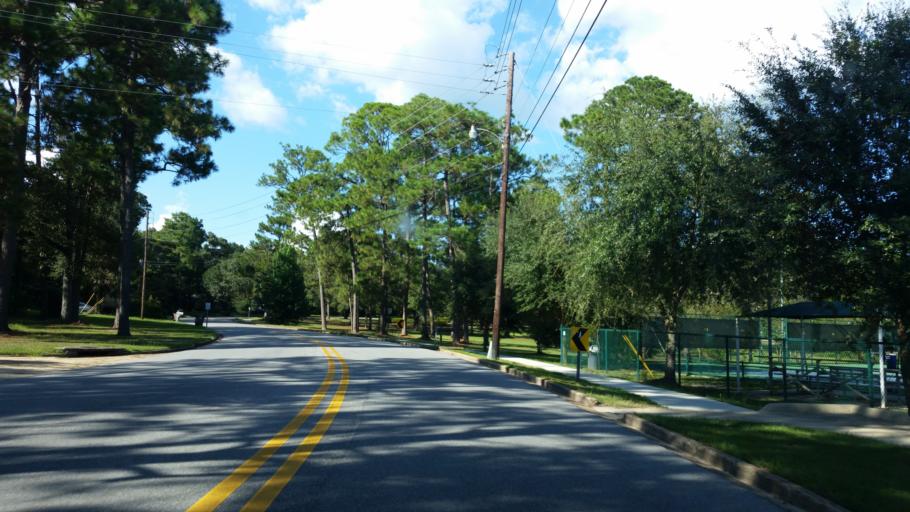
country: US
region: Alabama
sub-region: Mobile County
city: Prichard
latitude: 30.7086
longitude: -88.1633
